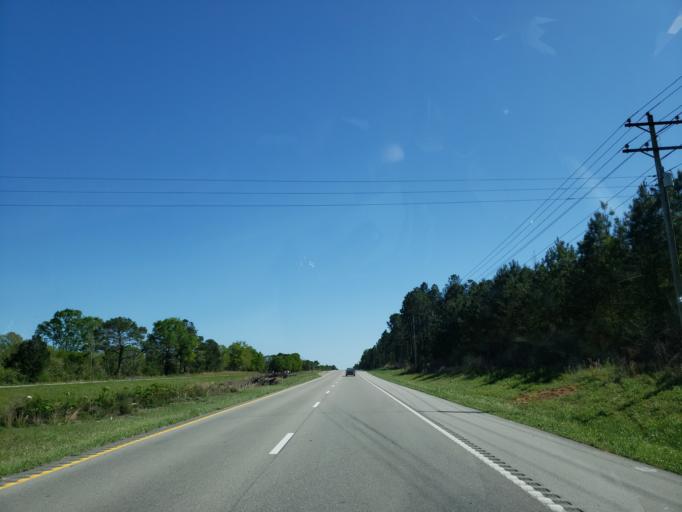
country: US
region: Mississippi
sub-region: Stone County
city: Wiggins
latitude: 30.9368
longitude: -89.1823
